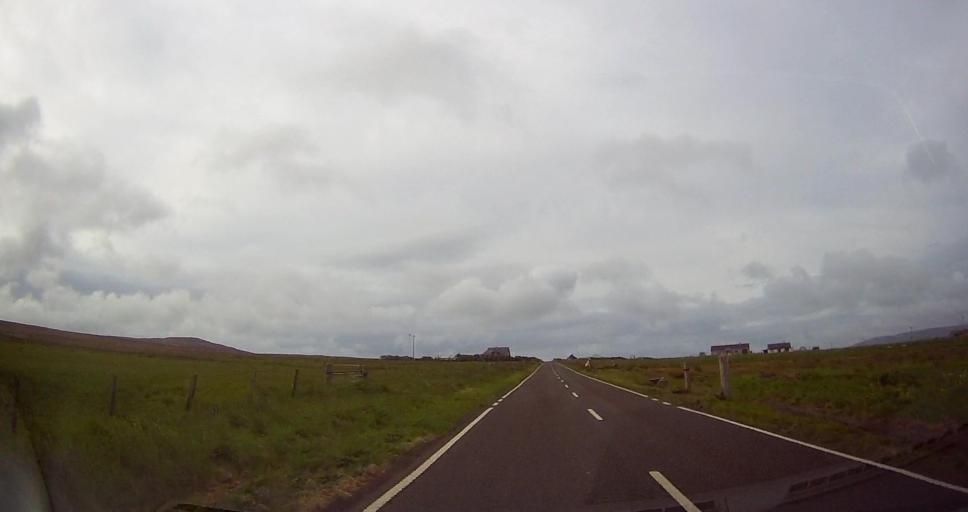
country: GB
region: Scotland
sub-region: Orkney Islands
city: Stromness
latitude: 58.9579
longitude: -3.2207
